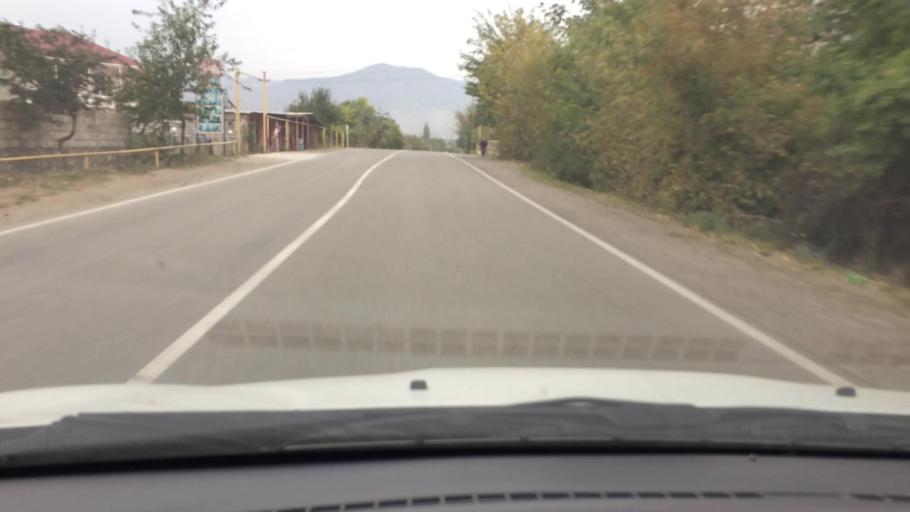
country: AM
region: Tavush
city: Bagratashen
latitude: 41.2362
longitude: 44.8069
